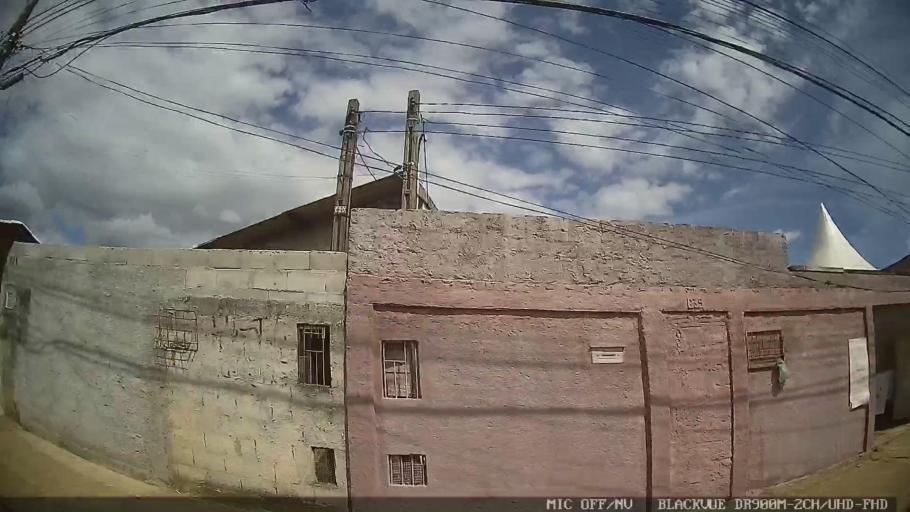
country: BR
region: Sao Paulo
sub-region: Mogi das Cruzes
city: Mogi das Cruzes
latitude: -23.5899
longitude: -46.2329
